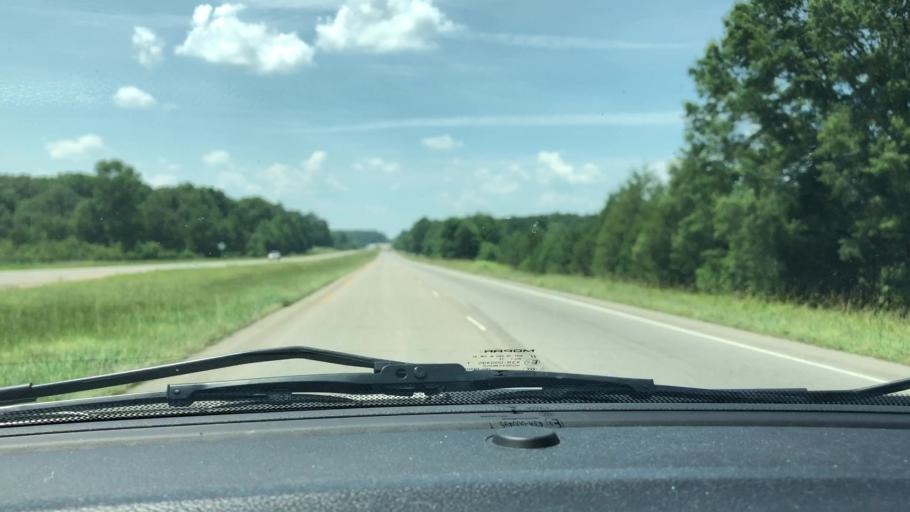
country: US
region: North Carolina
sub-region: Chatham County
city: Farmville
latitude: 35.6167
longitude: -79.3499
